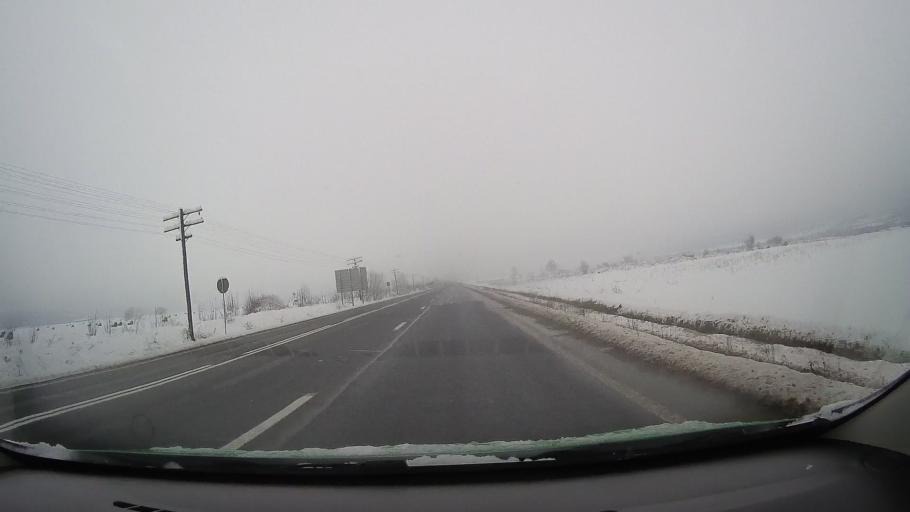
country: RO
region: Sibiu
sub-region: Oras Saliste
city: Saliste
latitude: 45.7986
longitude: 23.9044
